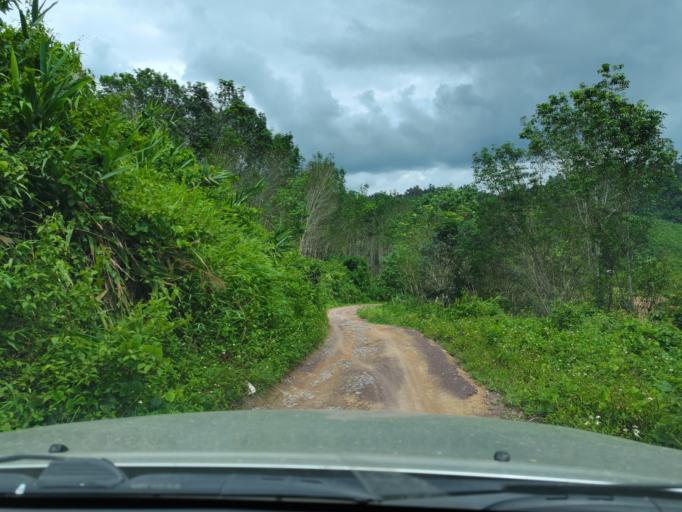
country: LA
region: Loungnamtha
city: Muang Long
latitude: 20.7023
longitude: 101.0155
